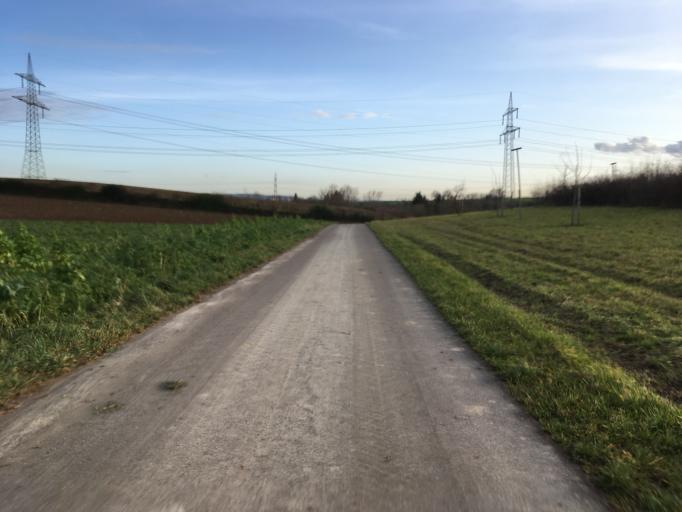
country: DE
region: Baden-Wuerttemberg
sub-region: Regierungsbezirk Stuttgart
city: Leingarten
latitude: 49.1657
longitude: 9.1546
